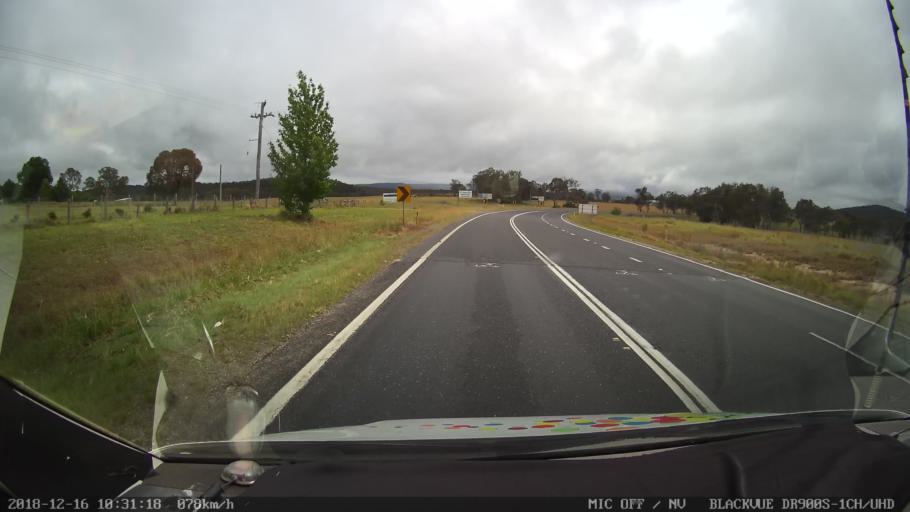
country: AU
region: New South Wales
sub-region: Tenterfield Municipality
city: Carrolls Creek
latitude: -29.0827
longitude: 152.0045
